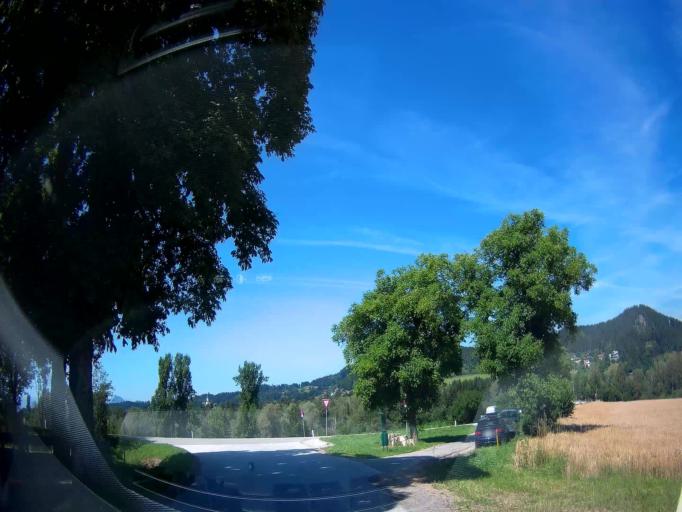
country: AT
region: Carinthia
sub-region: Politischer Bezirk Sankt Veit an der Glan
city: St. Georgen am Laengsee
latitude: 46.7819
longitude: 14.4280
